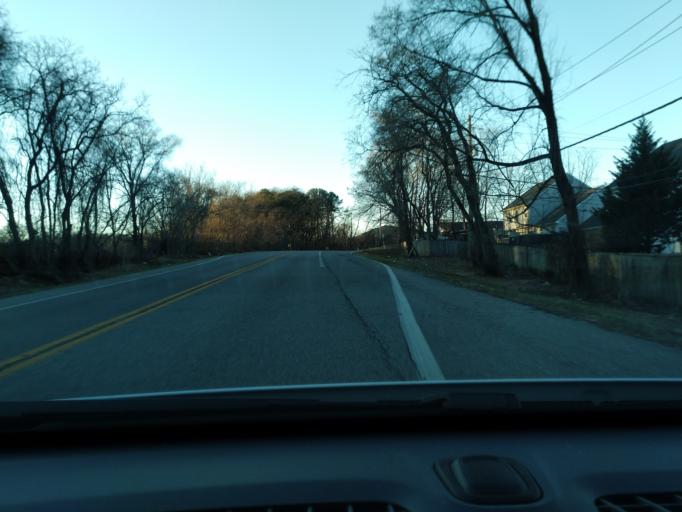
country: US
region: Maryland
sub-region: Anne Arundel County
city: Glen Burnie
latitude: 39.1585
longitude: -76.6015
